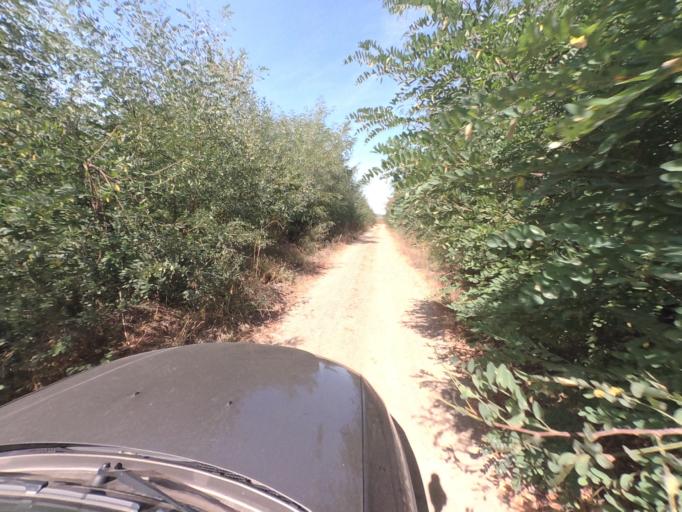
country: RO
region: Vaslui
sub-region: Comuna Costesti
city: Costesti
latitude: 46.5214
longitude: 27.7395
